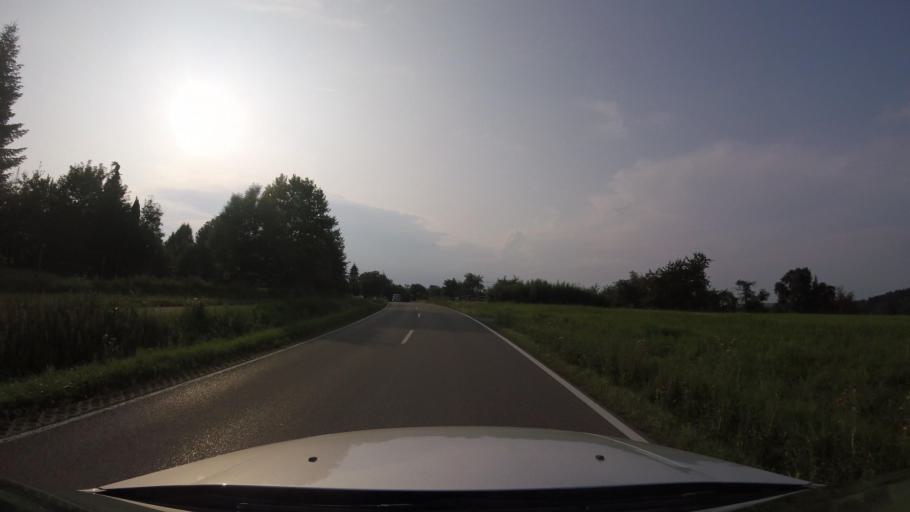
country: DE
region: Baden-Wuerttemberg
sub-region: Regierungsbezirk Stuttgart
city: Welzheim
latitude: 48.8541
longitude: 9.6296
